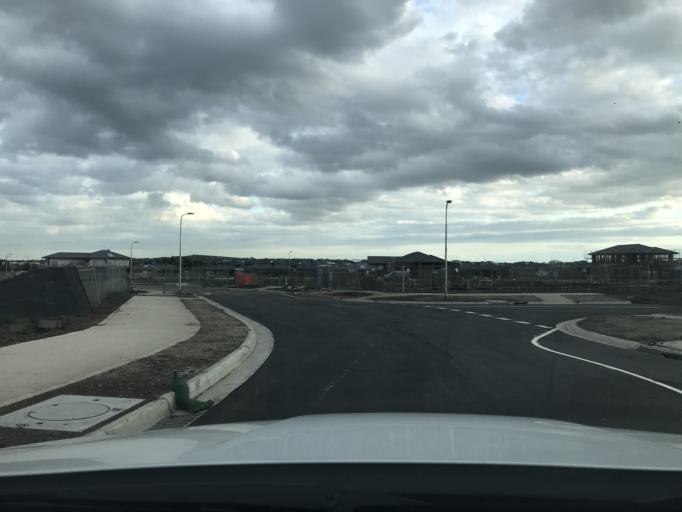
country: AU
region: Victoria
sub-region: Hume
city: Roxburgh Park
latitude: -37.5806
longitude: 144.8994
